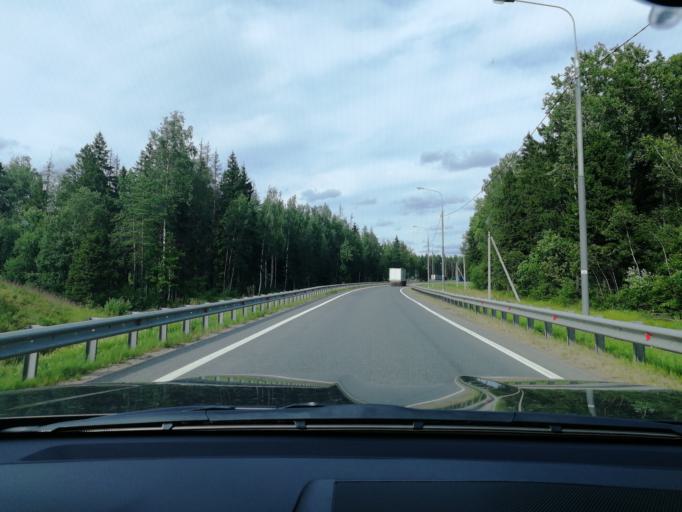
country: RU
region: Moskovskaya
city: Novyy Byt
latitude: 55.0351
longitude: 37.5614
